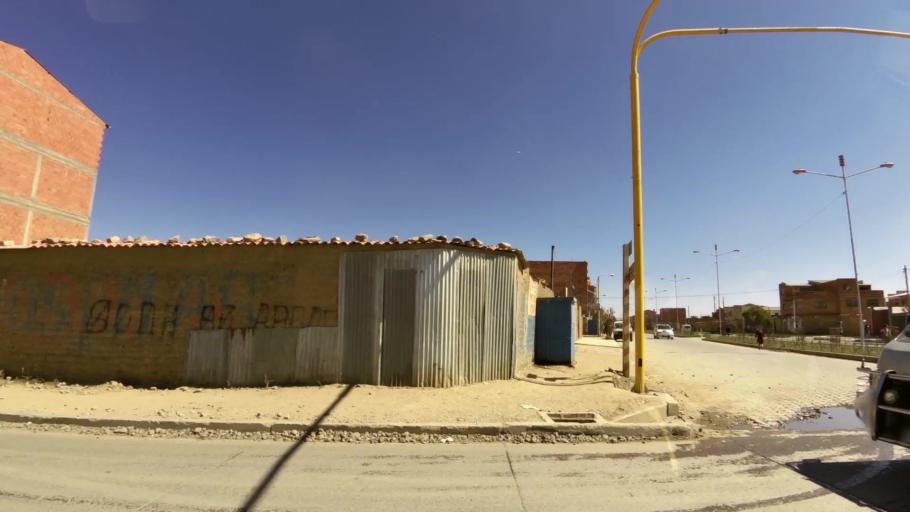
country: BO
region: La Paz
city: La Paz
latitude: -16.5054
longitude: -68.2111
